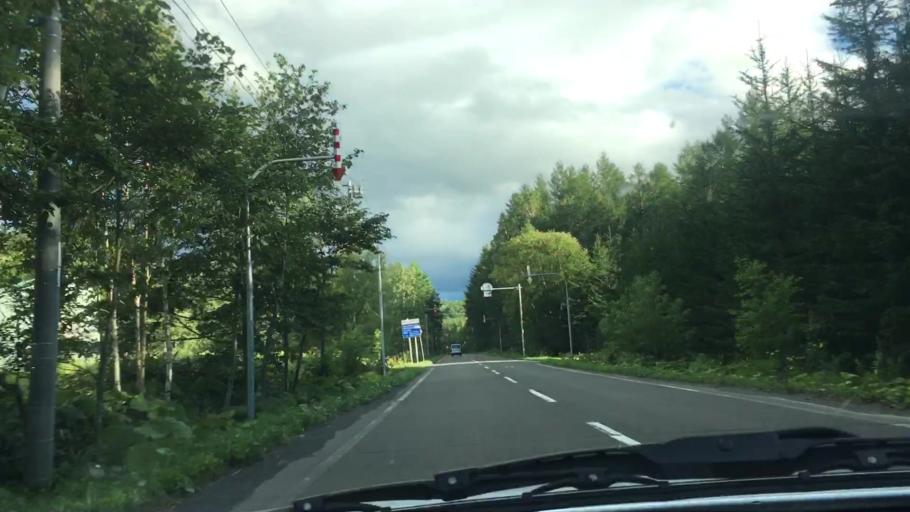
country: JP
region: Hokkaido
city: Shimo-furano
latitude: 43.1201
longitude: 142.6808
